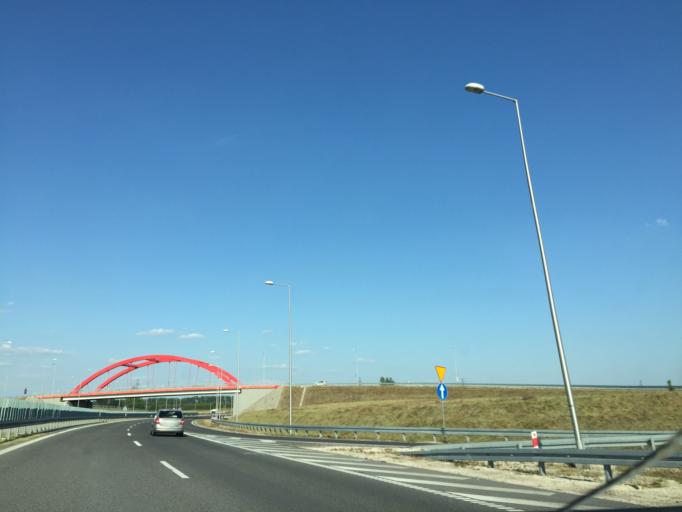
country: PL
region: Swietokrzyskie
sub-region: Powiat jedrzejowski
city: Jedrzejow
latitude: 50.6232
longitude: 20.2857
